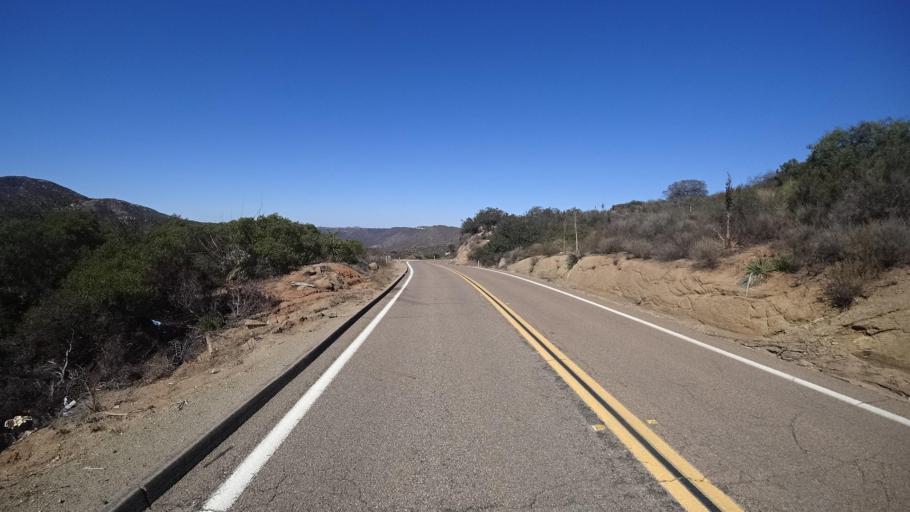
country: US
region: California
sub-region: San Diego County
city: Alpine
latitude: 32.7821
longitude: -116.7196
